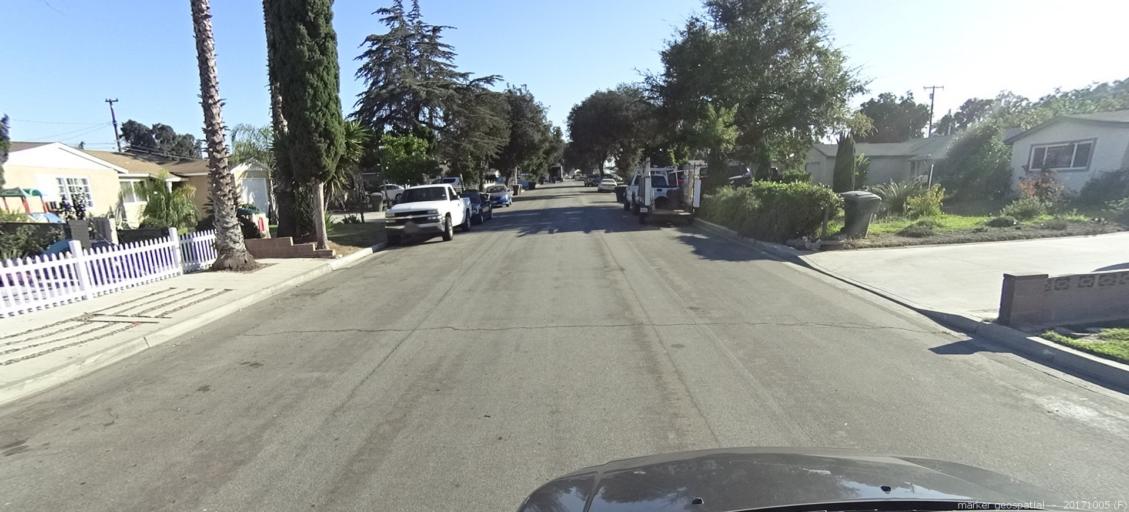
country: US
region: California
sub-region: Orange County
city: Stanton
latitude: 33.7945
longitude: -117.9823
